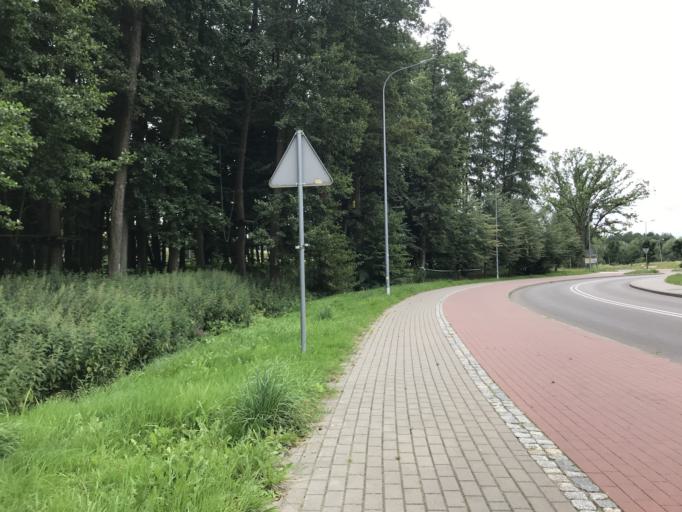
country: PL
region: Warmian-Masurian Voivodeship
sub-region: Powiat elblaski
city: Gronowo Gorne
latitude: 54.1703
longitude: 19.4418
